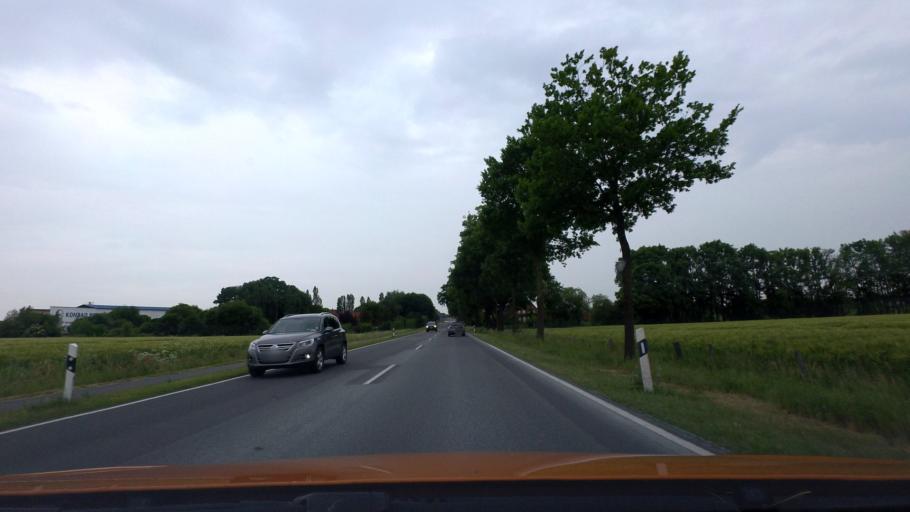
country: DE
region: Lower Saxony
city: Asendorf
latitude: 52.7632
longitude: 9.0126
